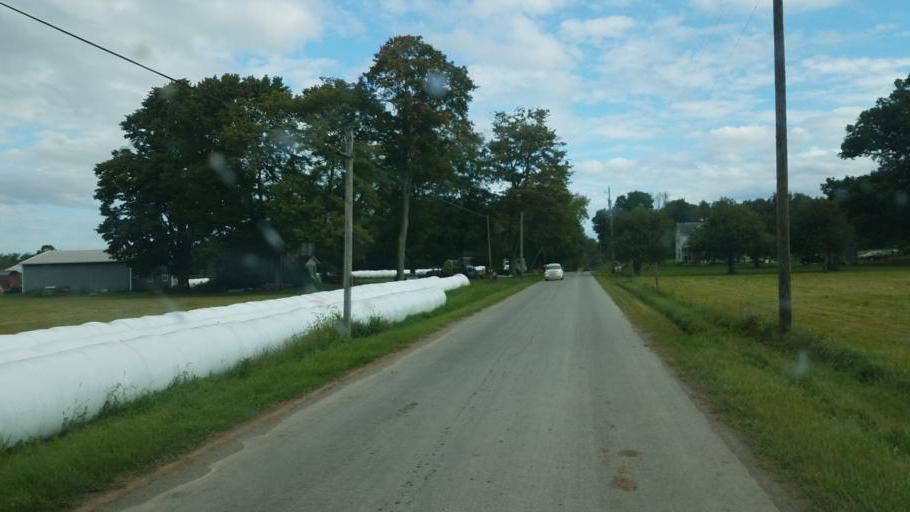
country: US
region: Pennsylvania
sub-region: Mercer County
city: Greenville
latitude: 41.4964
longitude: -80.3482
